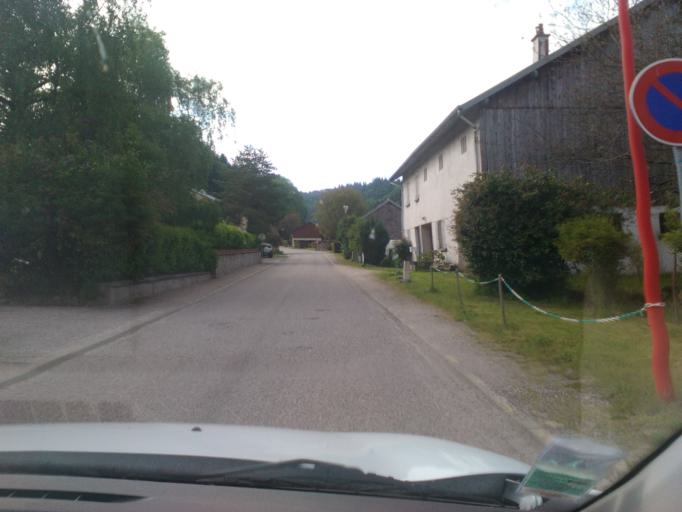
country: FR
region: Lorraine
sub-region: Departement des Vosges
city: Le Tholy
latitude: 48.1190
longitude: 6.7315
